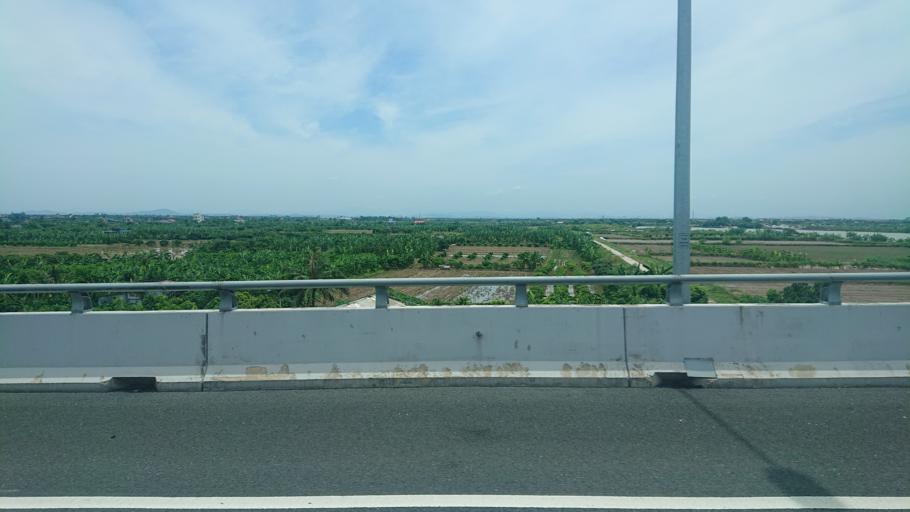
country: VN
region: Hai Phong
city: An Lao
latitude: 20.8089
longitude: 106.5100
